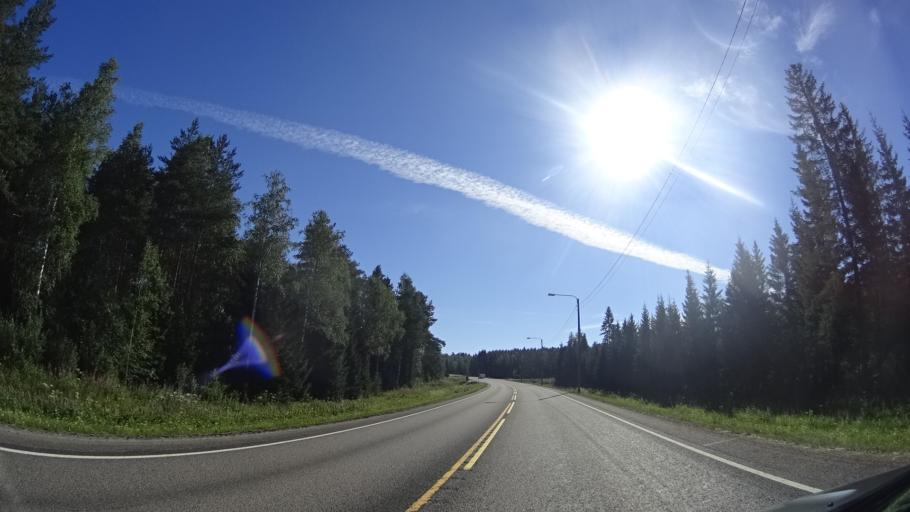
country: FI
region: Central Finland
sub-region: Jyvaeskylae
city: Petaejaevesi
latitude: 62.2703
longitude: 25.3357
